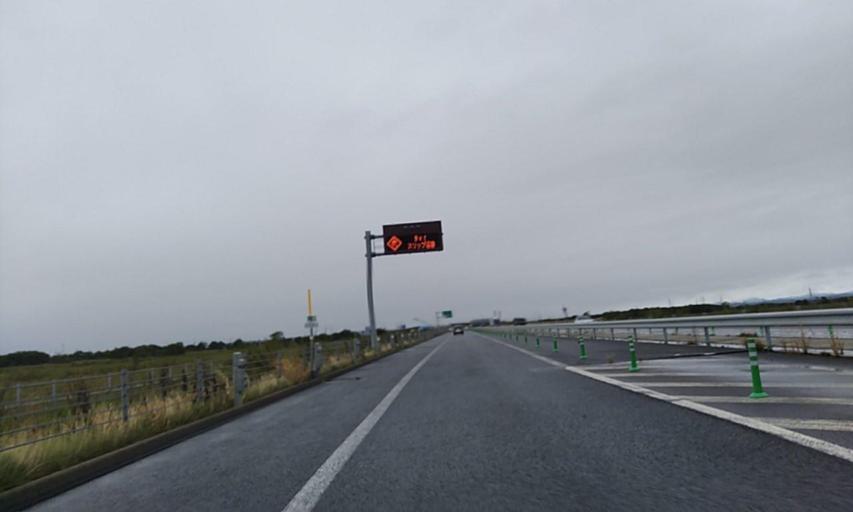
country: JP
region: Hokkaido
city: Kushiro
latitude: 43.0372
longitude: 144.3368
